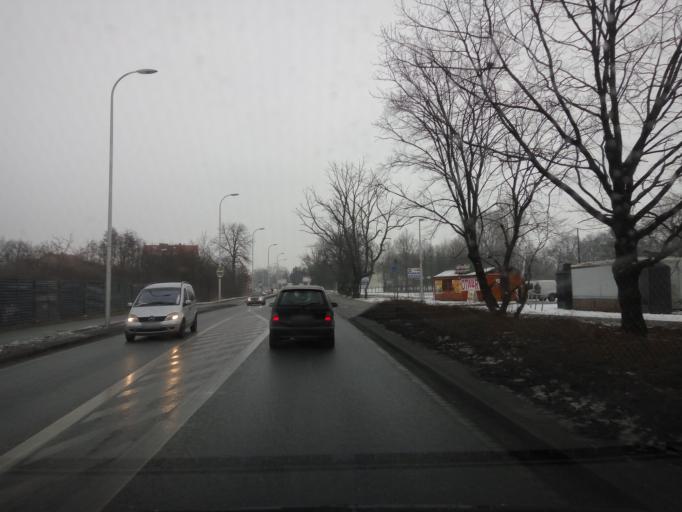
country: PL
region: Lower Silesian Voivodeship
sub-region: Powiat wroclawski
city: Bielany Wroclawskie
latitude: 51.0608
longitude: 16.9989
